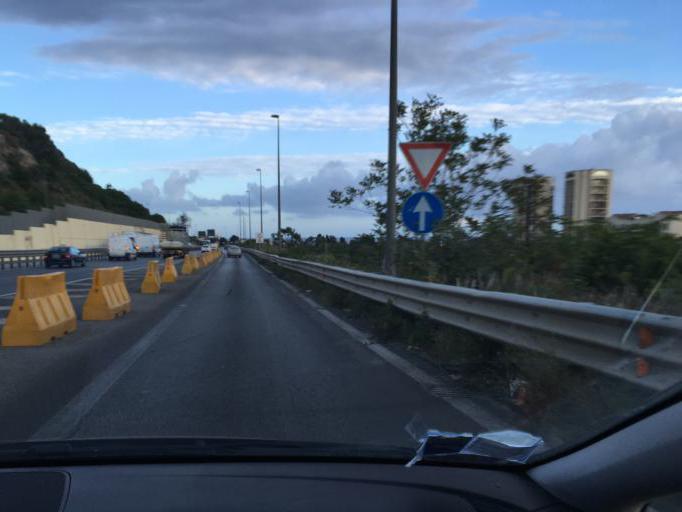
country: IT
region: Sicily
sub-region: Palermo
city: Isola delle Femmine
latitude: 38.1921
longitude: 13.2814
